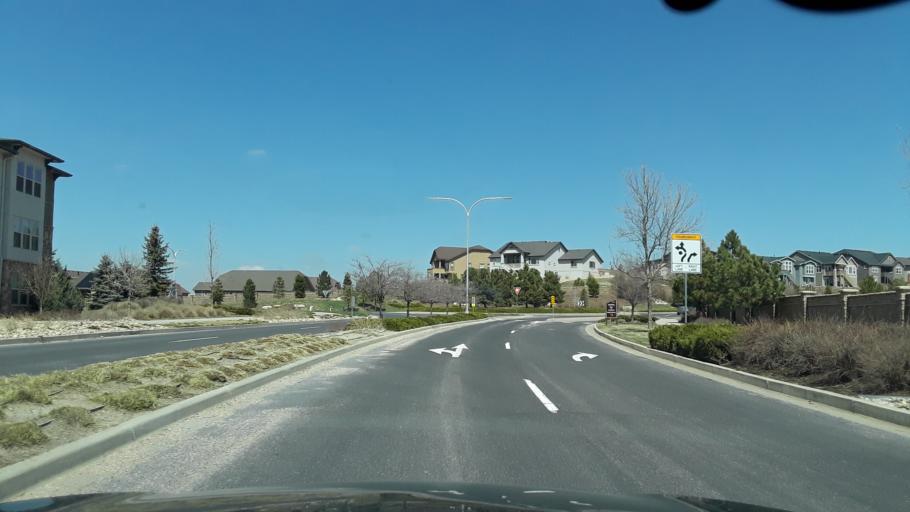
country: US
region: Colorado
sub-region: El Paso County
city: Black Forest
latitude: 38.9750
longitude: -104.7405
